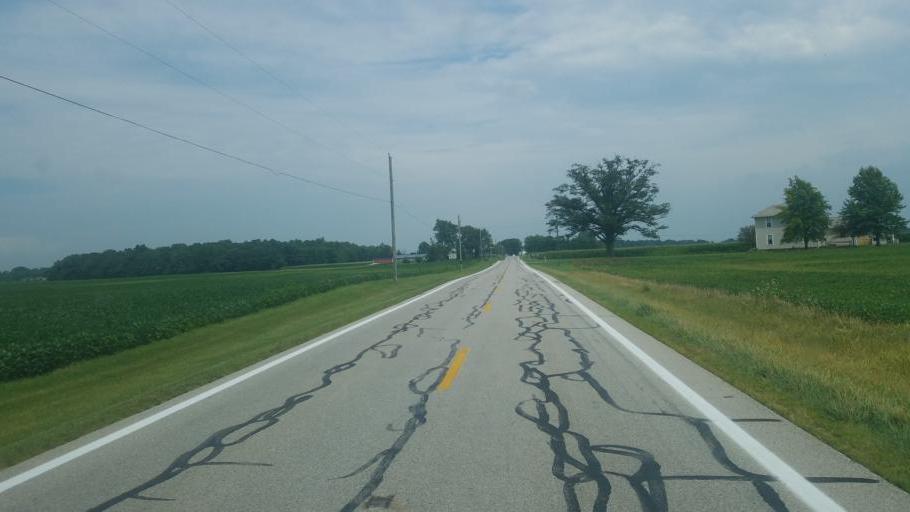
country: US
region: Ohio
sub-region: Union County
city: Richwood
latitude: 40.3507
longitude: -83.3656
